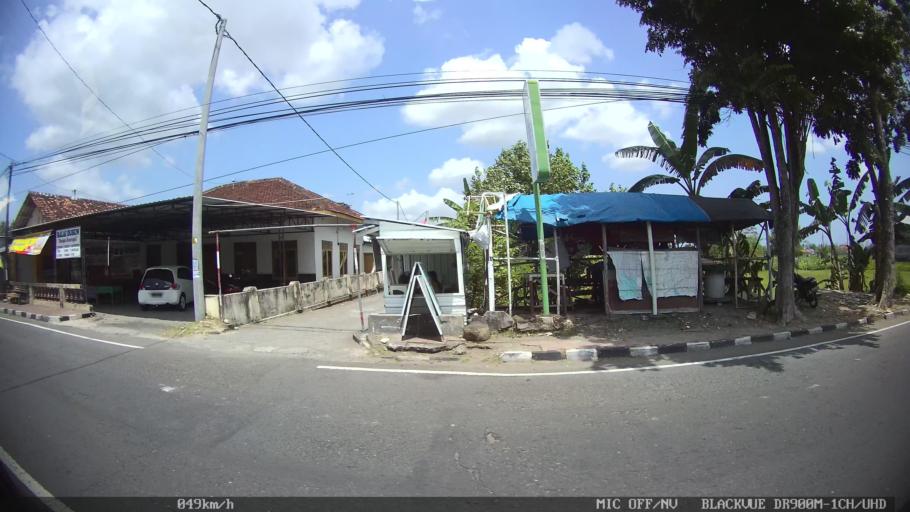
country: ID
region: Daerah Istimewa Yogyakarta
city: Bantul
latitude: -7.8918
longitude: 110.3291
